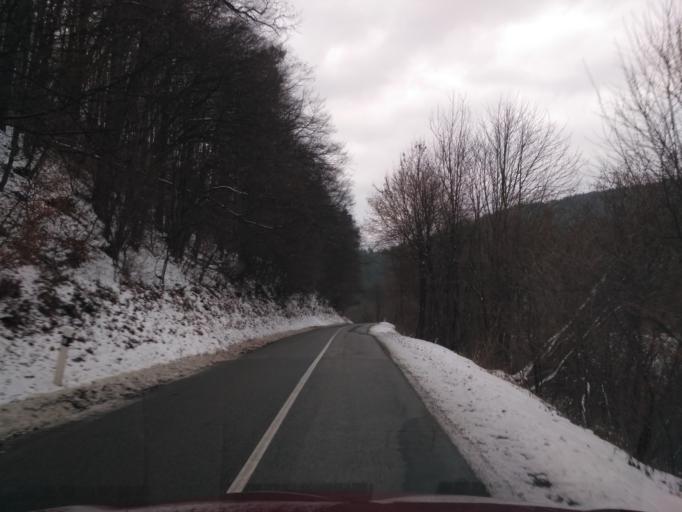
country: SK
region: Presovsky
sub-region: Okres Presov
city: Presov
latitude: 48.9632
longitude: 21.0999
